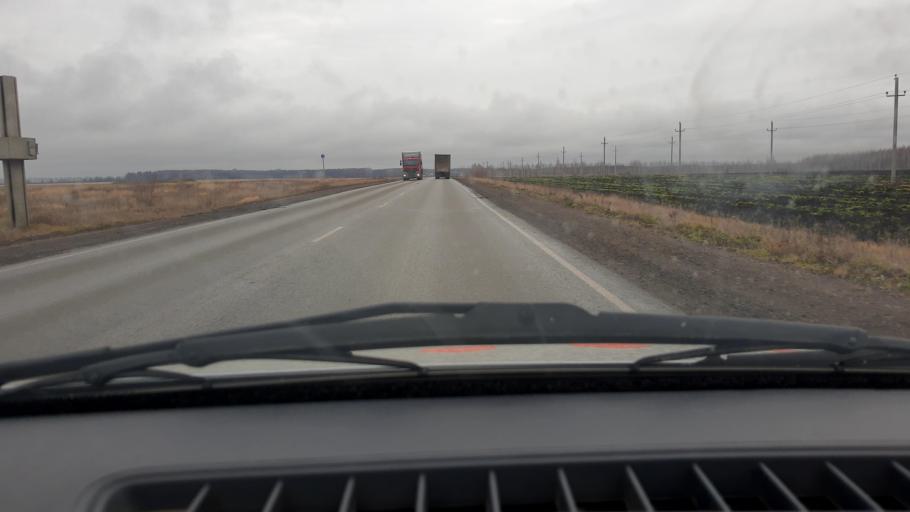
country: RU
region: Bashkortostan
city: Iglino
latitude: 54.7560
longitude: 56.2807
